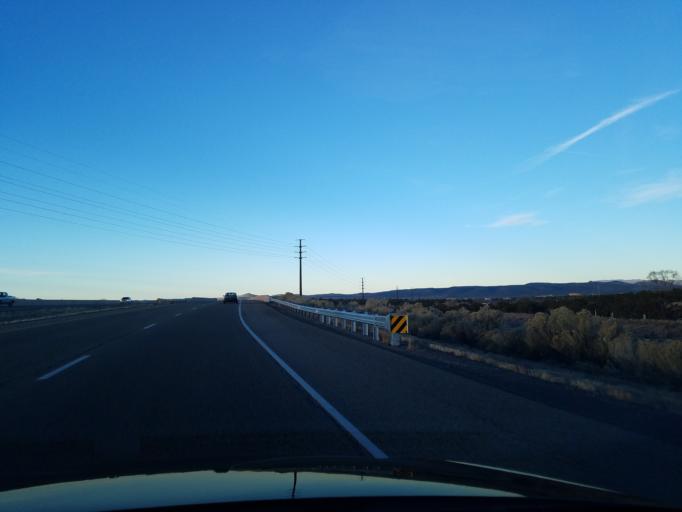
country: US
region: New Mexico
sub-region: Santa Fe County
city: Agua Fria
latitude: 35.6679
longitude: -106.0208
